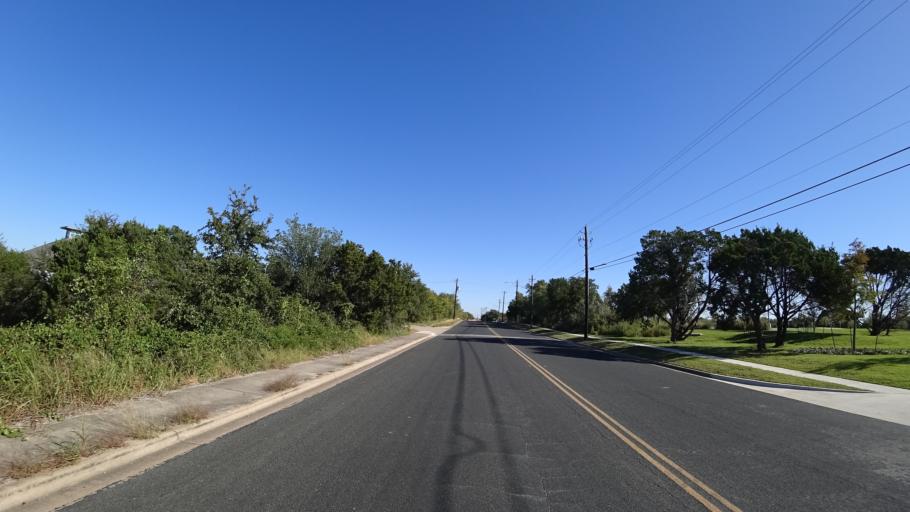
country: US
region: Texas
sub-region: Travis County
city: Austin
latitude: 30.2813
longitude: -97.6727
